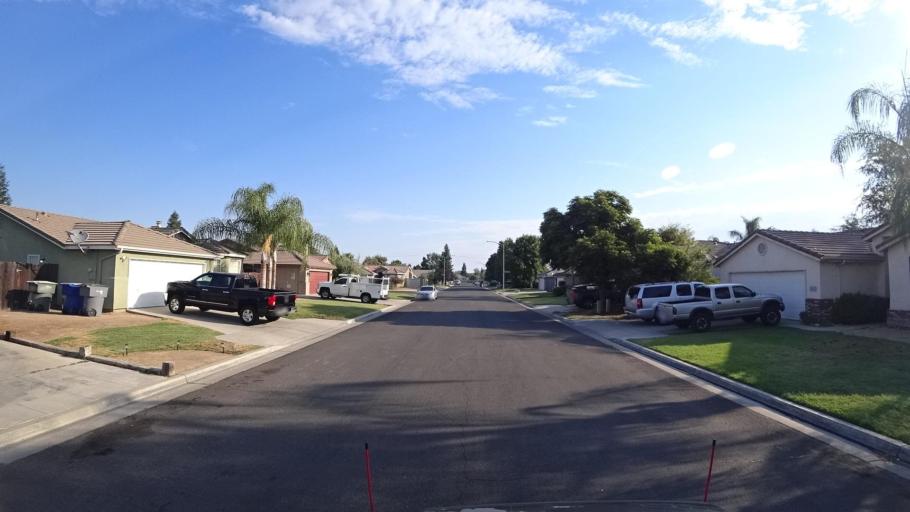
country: US
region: California
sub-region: Fresno County
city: Sunnyside
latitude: 36.7124
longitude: -119.6938
